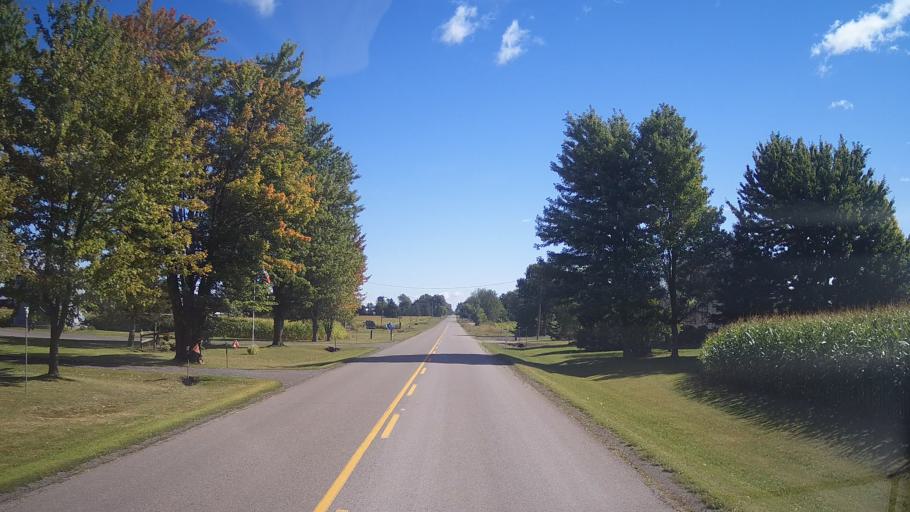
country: CA
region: Ontario
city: Prescott
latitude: 44.9151
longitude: -75.3676
